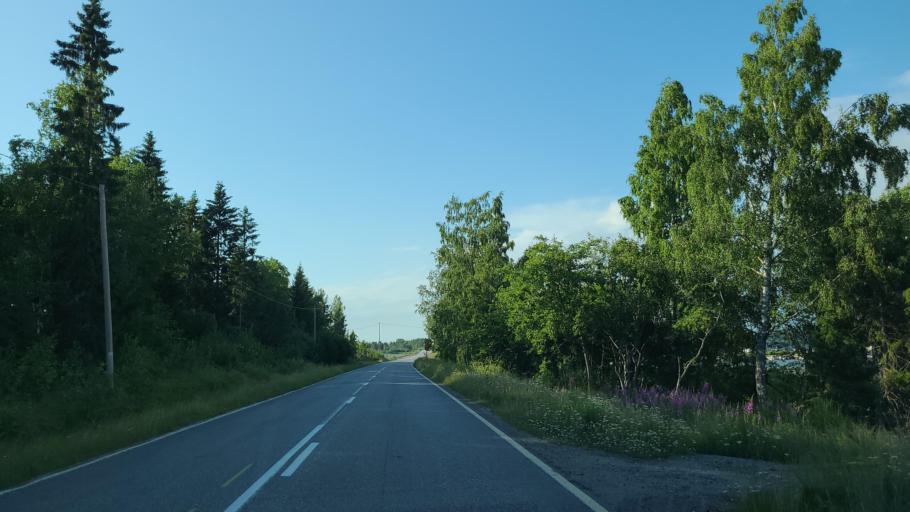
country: FI
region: Ostrobothnia
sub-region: Vaasa
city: Replot
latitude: 63.2698
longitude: 21.3465
